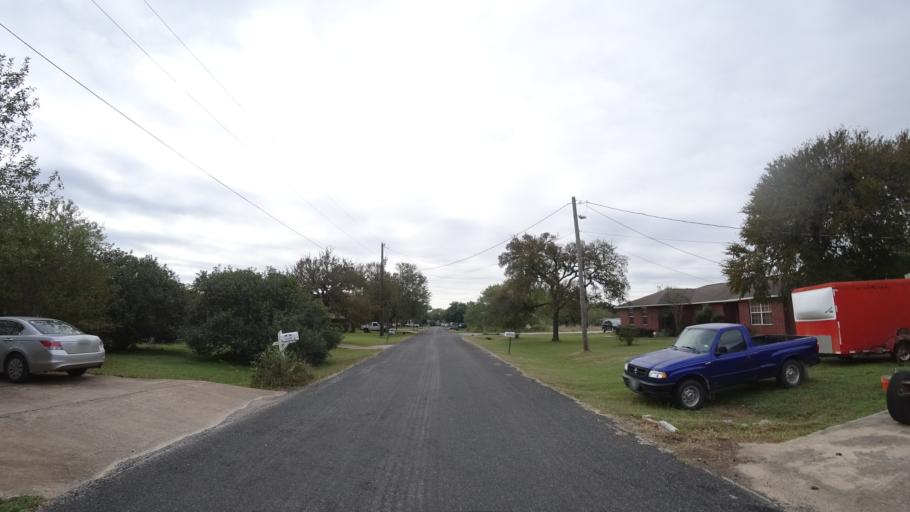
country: US
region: Texas
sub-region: Travis County
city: Shady Hollow
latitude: 30.1474
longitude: -97.8774
